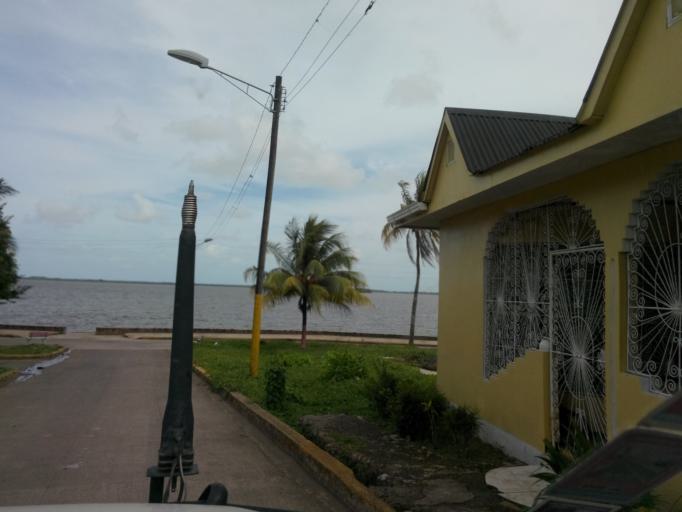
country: NI
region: Atlantico Sur
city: Bluefields
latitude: 11.9997
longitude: -83.7642
